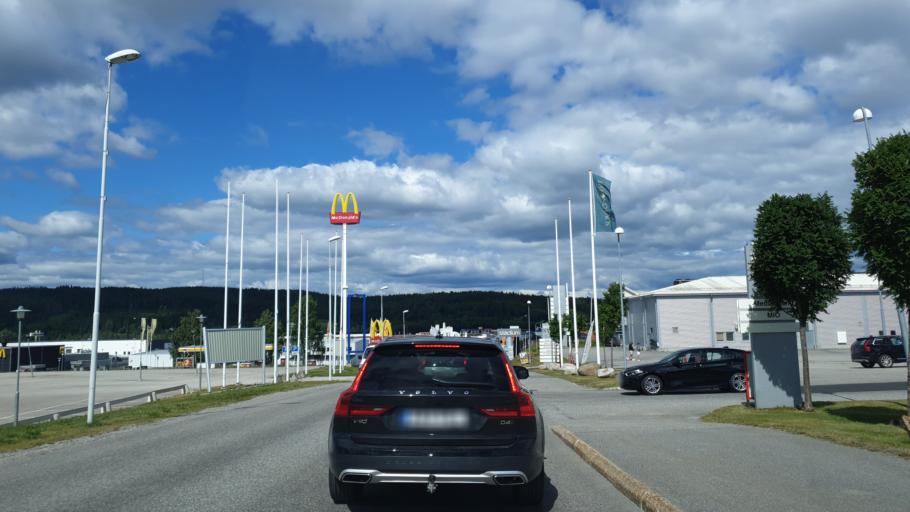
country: SE
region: Vaesternorrland
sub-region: Sundsvalls Kommun
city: Sundsbruk
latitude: 62.4404
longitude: 17.3314
